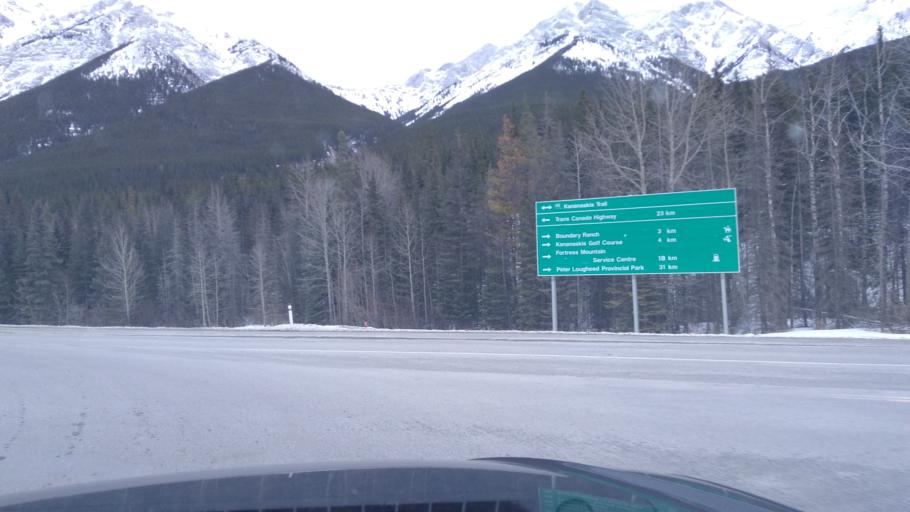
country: CA
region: Alberta
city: Canmore
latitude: 50.9321
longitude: -115.1269
